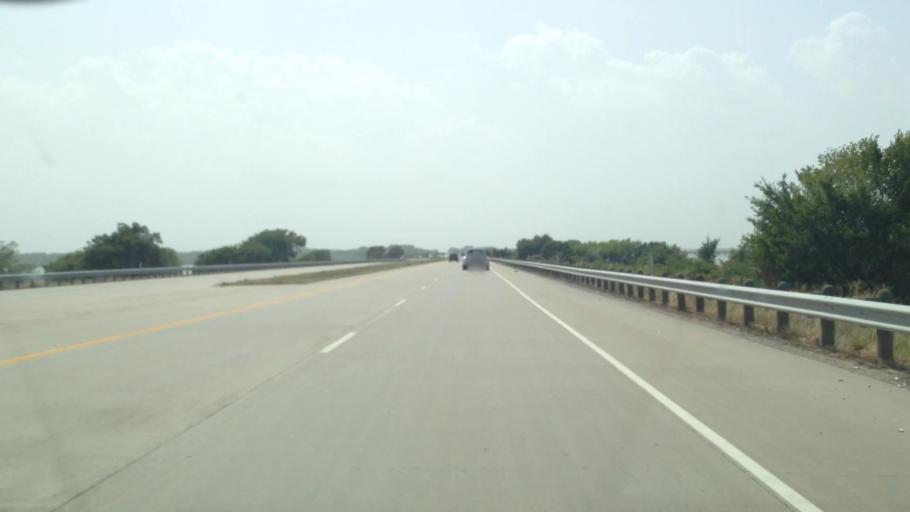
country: US
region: Texas
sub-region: Collin County
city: Farmersville
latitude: 33.1607
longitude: -96.4173
